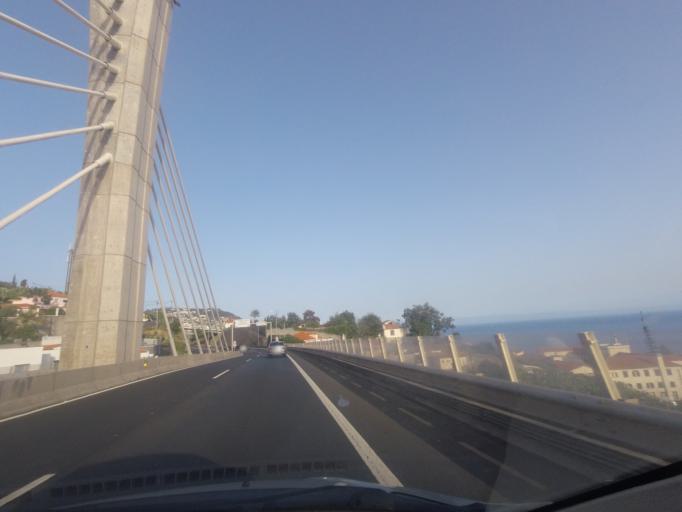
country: PT
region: Madeira
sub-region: Funchal
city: Nossa Senhora do Monte
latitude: 32.6619
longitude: -16.9067
